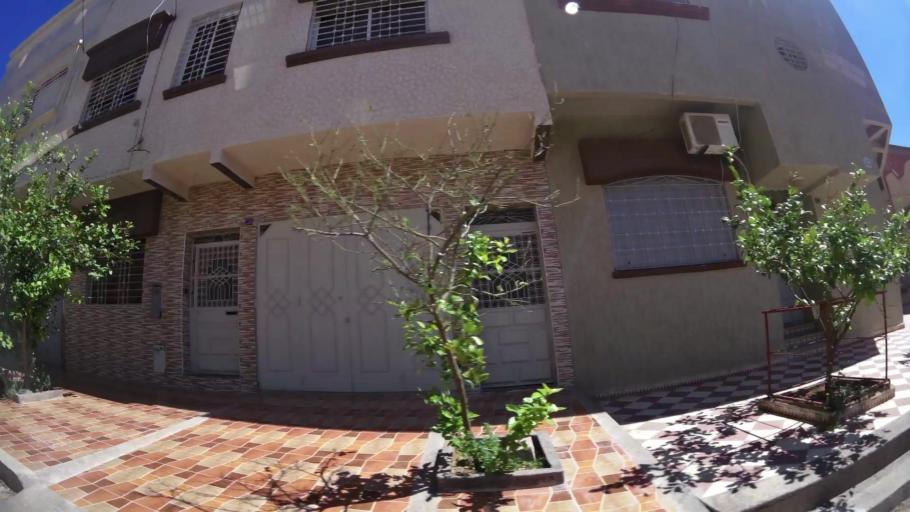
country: MA
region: Oriental
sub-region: Oujda-Angad
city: Oujda
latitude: 34.6624
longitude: -1.8781
